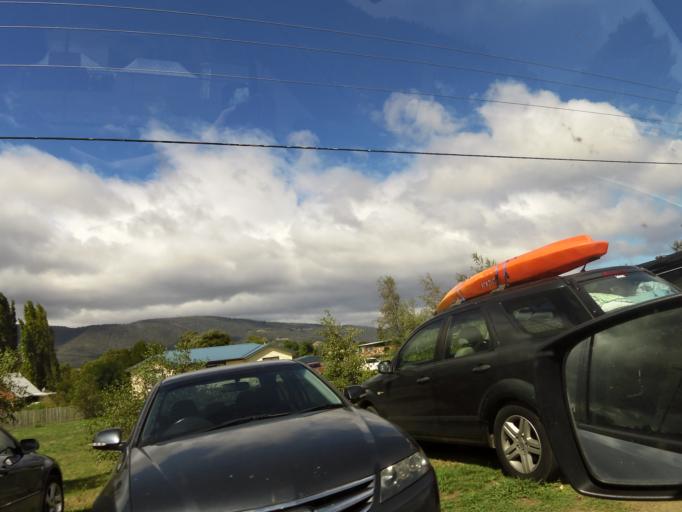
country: AU
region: Tasmania
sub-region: Huon Valley
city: Huonville
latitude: -43.0075
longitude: 147.0406
